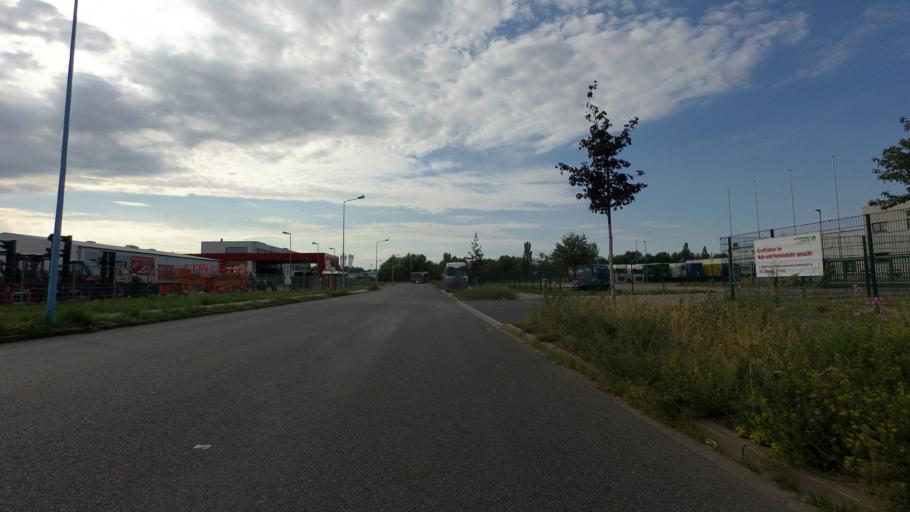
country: DE
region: Brandenburg
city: Wustermark
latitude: 52.5627
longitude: 12.9776
